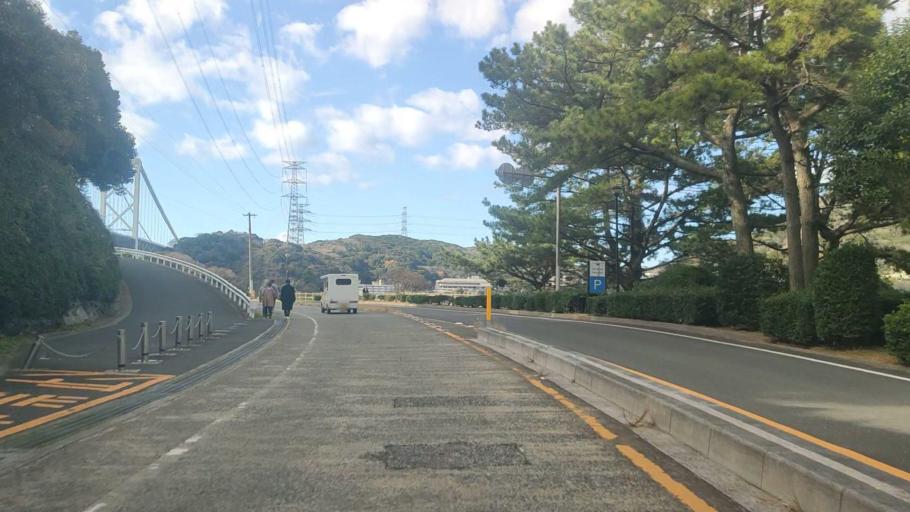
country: JP
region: Yamaguchi
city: Shimonoseki
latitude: 33.9616
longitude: 130.9643
